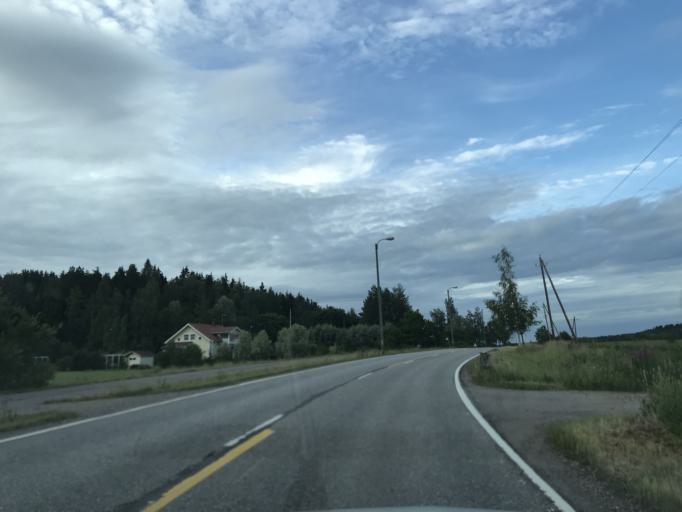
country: FI
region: Uusimaa
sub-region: Helsinki
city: Nurmijaervi
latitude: 60.3926
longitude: 24.6431
